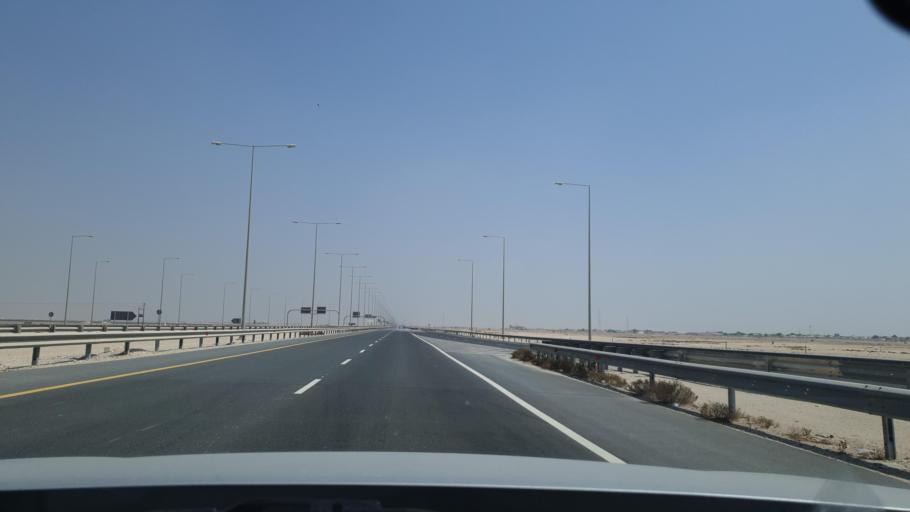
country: QA
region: Baladiyat az Za`ayin
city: Az Za`ayin
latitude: 25.6175
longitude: 51.3745
